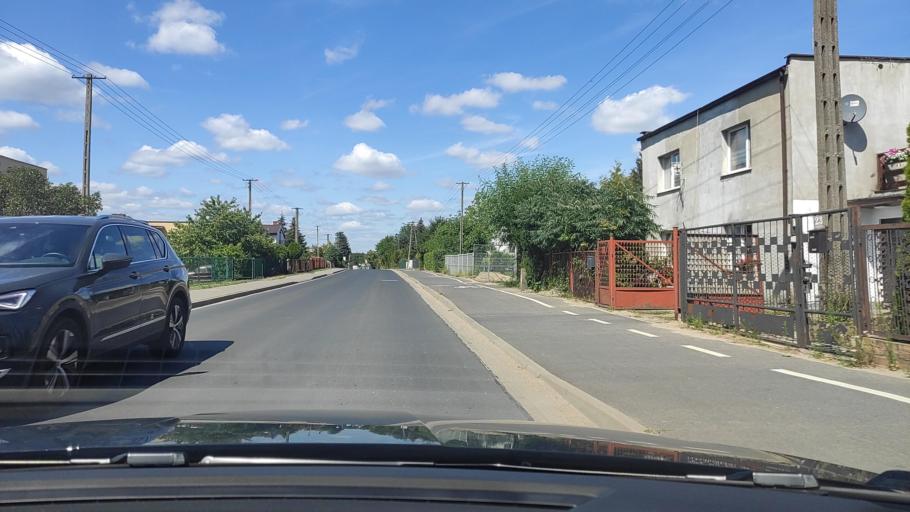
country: PL
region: Greater Poland Voivodeship
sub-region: Powiat poznanski
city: Kostrzyn
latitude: 52.4629
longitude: 17.1691
